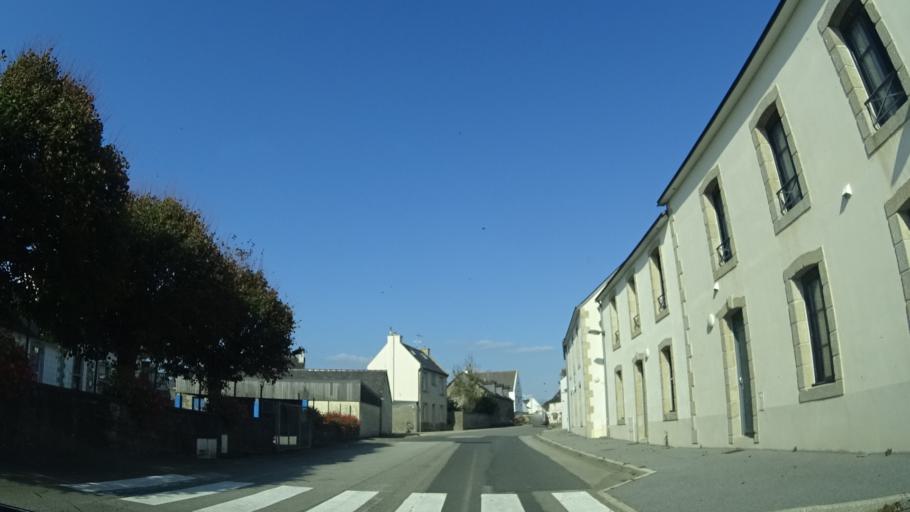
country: FR
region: Brittany
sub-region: Departement du Finistere
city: Cast
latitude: 48.1554
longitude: -4.1404
